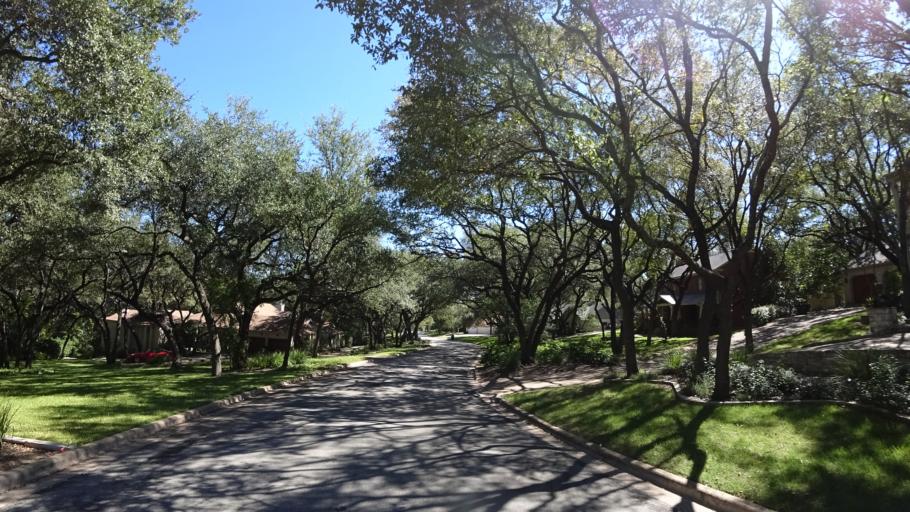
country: US
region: Texas
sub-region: Travis County
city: West Lake Hills
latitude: 30.3092
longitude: -97.7860
